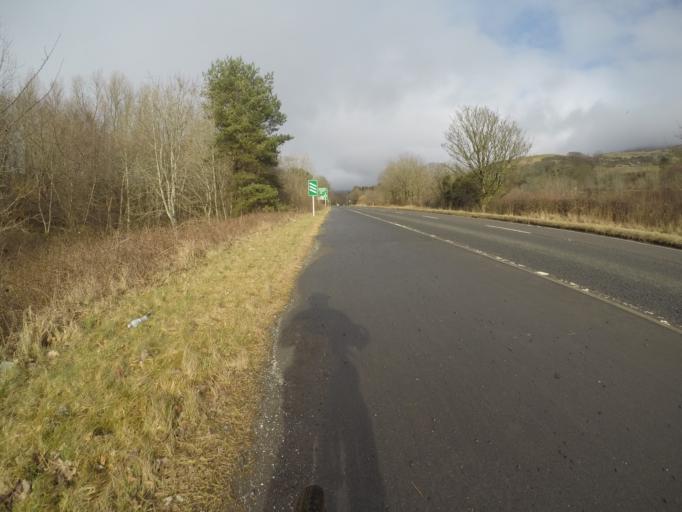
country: GB
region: Scotland
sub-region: North Ayrshire
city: Fairlie
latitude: 55.7411
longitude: -4.8601
